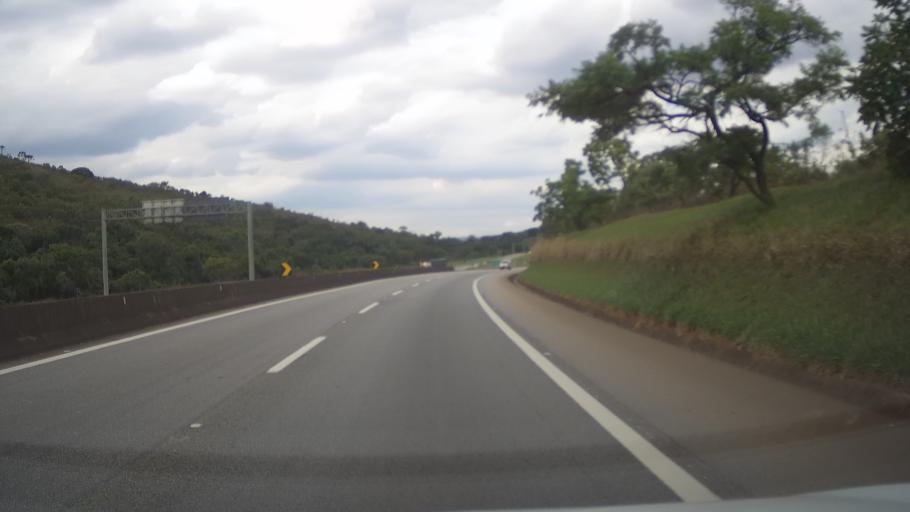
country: BR
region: Minas Gerais
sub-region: Tres Coracoes
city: Tres Coracoes
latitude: -21.5292
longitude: -45.2299
